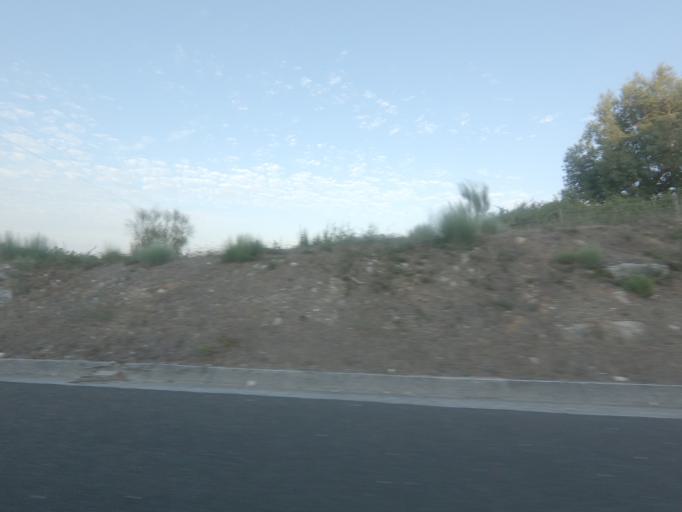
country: PT
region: Leiria
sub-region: Leiria
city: Santa Catarina da Serra
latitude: 39.6774
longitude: -8.6837
